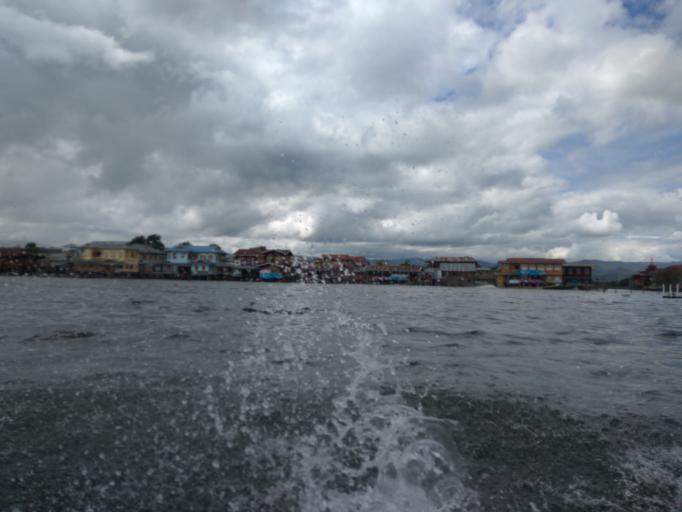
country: MM
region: Shan
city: Taunggyi
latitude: 20.4578
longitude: 96.9083
